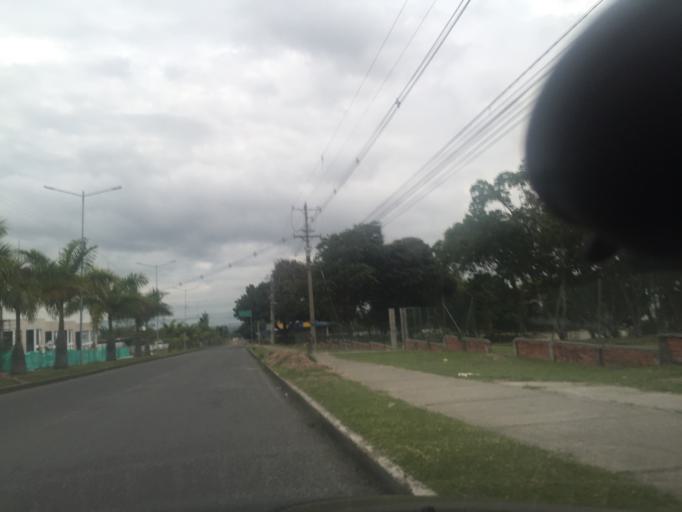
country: CO
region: Quindio
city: Armenia
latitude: 4.5145
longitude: -75.6980
